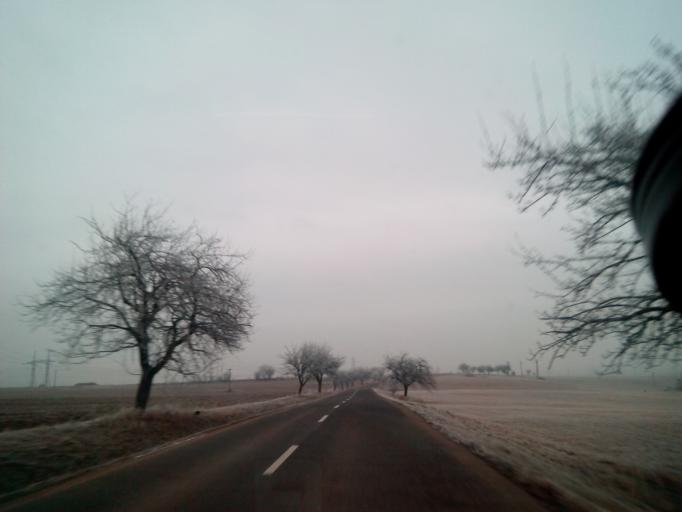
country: SK
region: Presovsky
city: Lubica
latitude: 48.9900
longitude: 20.4296
